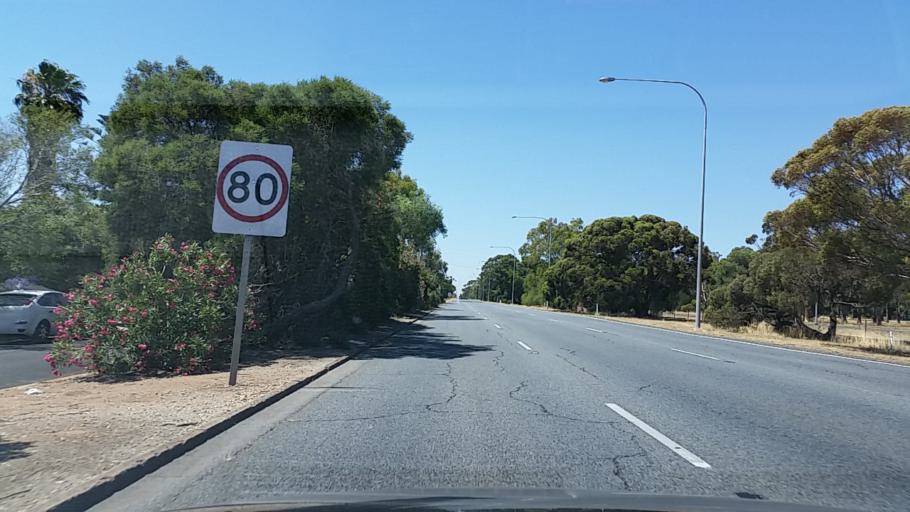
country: AU
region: South Australia
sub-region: Playford
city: Smithfield
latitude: -34.6985
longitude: 138.6838
